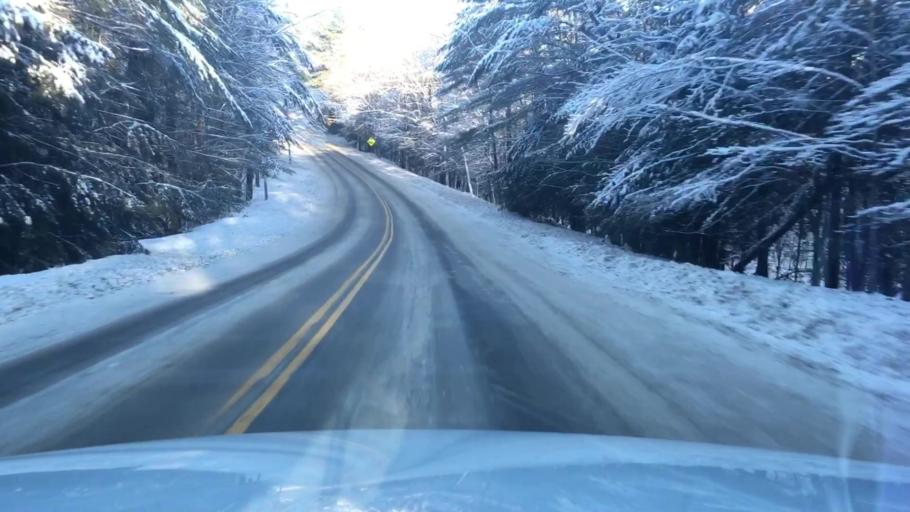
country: US
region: Maine
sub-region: Kennebec County
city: Readfield
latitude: 44.4320
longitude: -69.9643
